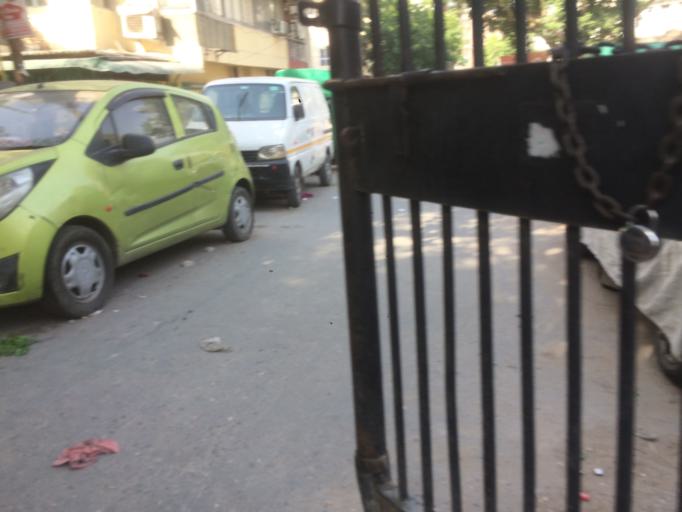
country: IN
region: Uttar Pradesh
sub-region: Gautam Buddha Nagar
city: Noida
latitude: 28.5807
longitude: 77.2632
